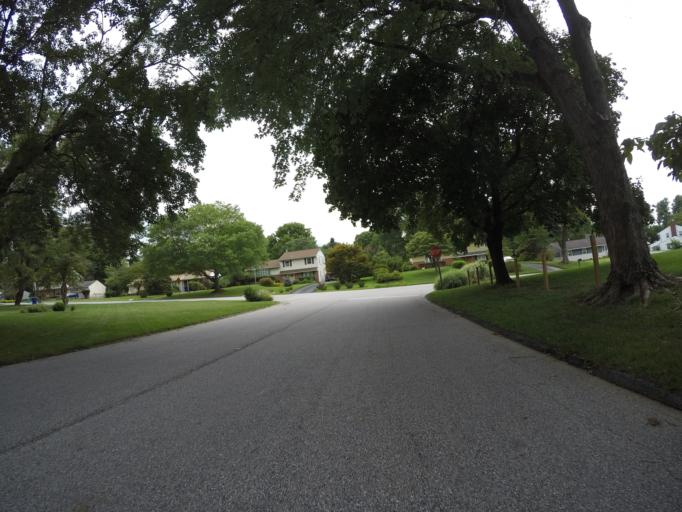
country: US
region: Maryland
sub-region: Howard County
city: Columbia
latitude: 39.2404
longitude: -76.8283
